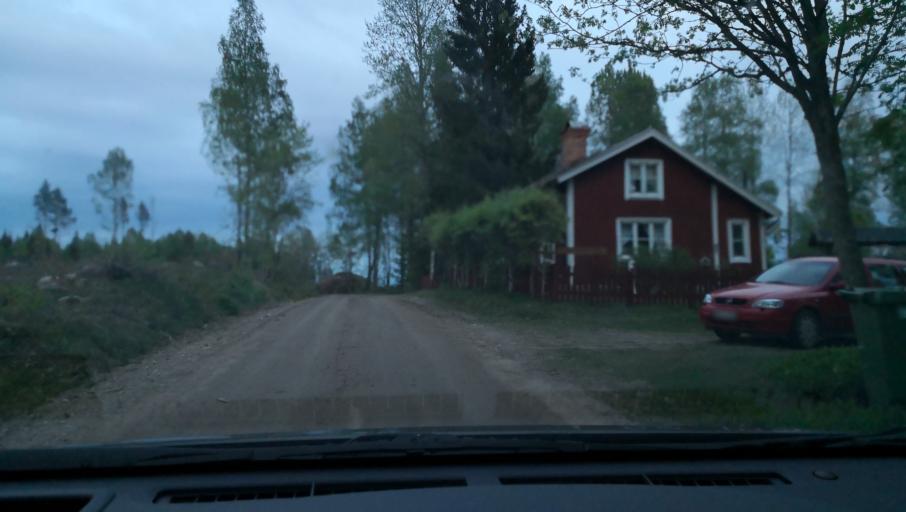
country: SE
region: Vaestmanland
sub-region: Skinnskattebergs Kommun
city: Skinnskatteberg
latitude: 59.7298
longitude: 15.4869
